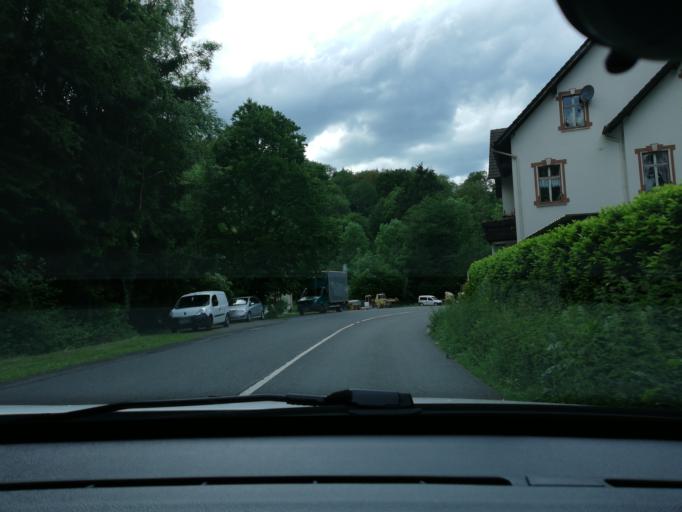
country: DE
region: North Rhine-Westphalia
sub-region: Regierungsbezirk Arnsberg
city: Schalksmuhle
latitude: 51.2344
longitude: 7.5574
